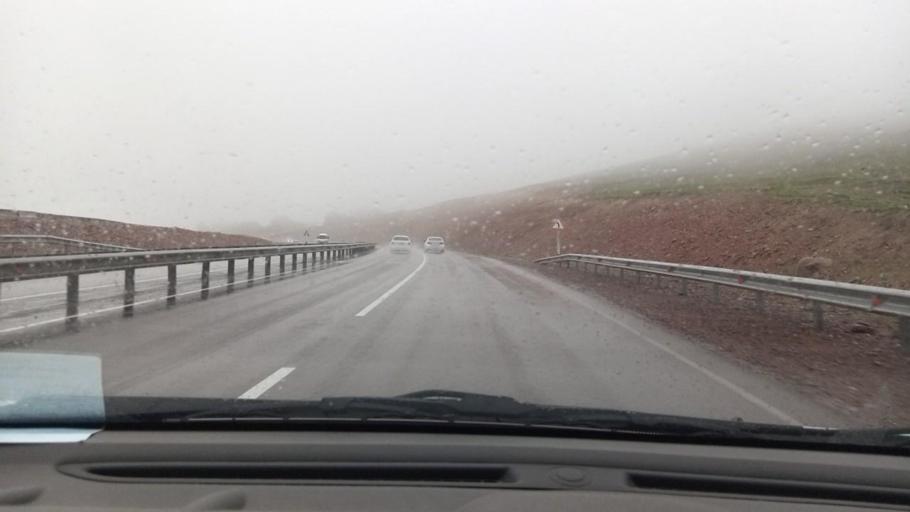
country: UZ
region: Toshkent
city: Angren
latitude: 41.0612
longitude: 70.1825
